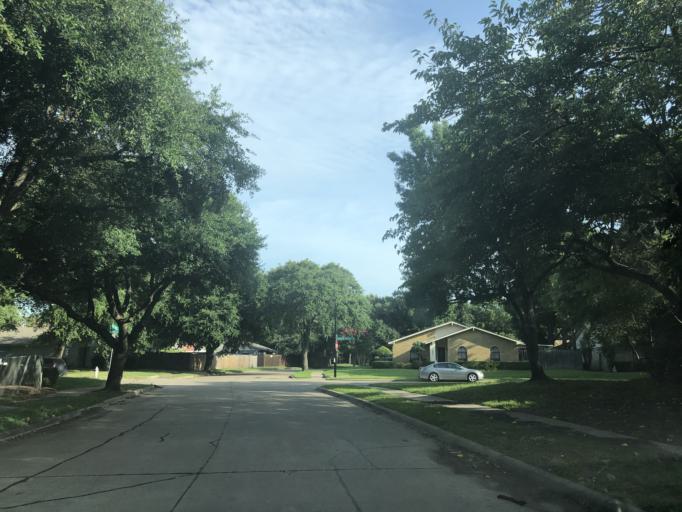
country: US
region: Texas
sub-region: Dallas County
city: Sunnyvale
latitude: 32.8391
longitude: -96.5863
